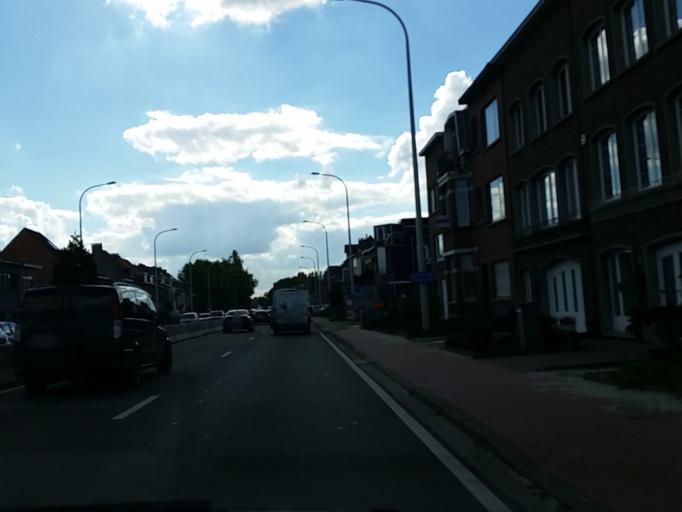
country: BE
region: Flanders
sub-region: Provincie Antwerpen
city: Wijnegem
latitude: 51.2207
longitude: 4.4977
